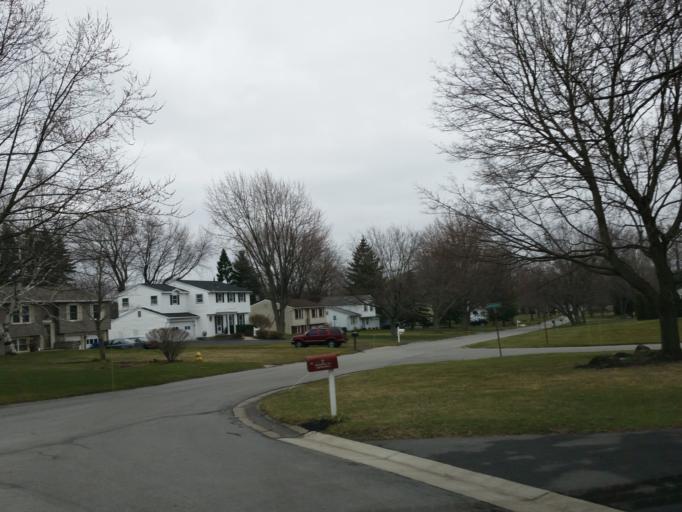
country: US
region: New York
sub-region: Monroe County
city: Scottsville
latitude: 43.1111
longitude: -77.7592
